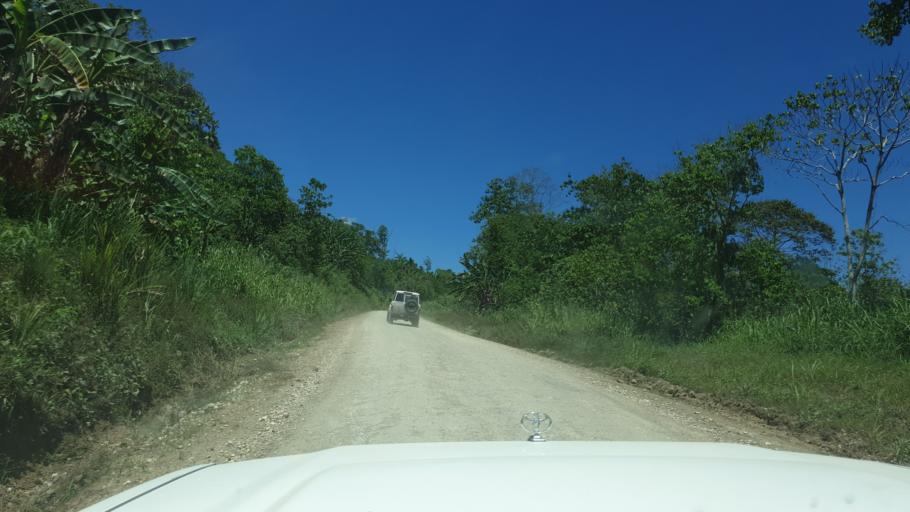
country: PG
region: Madang
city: Madang
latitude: -5.5225
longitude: 145.4151
